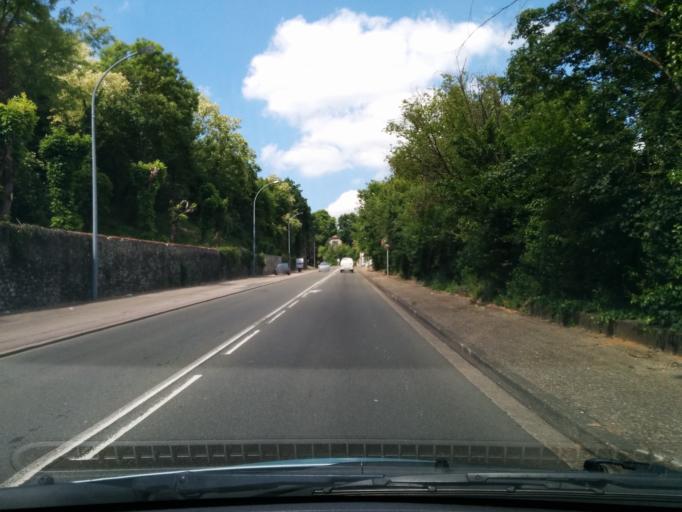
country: FR
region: Ile-de-France
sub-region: Departement des Yvelines
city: Freneuse
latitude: 49.0241
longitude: 1.6111
